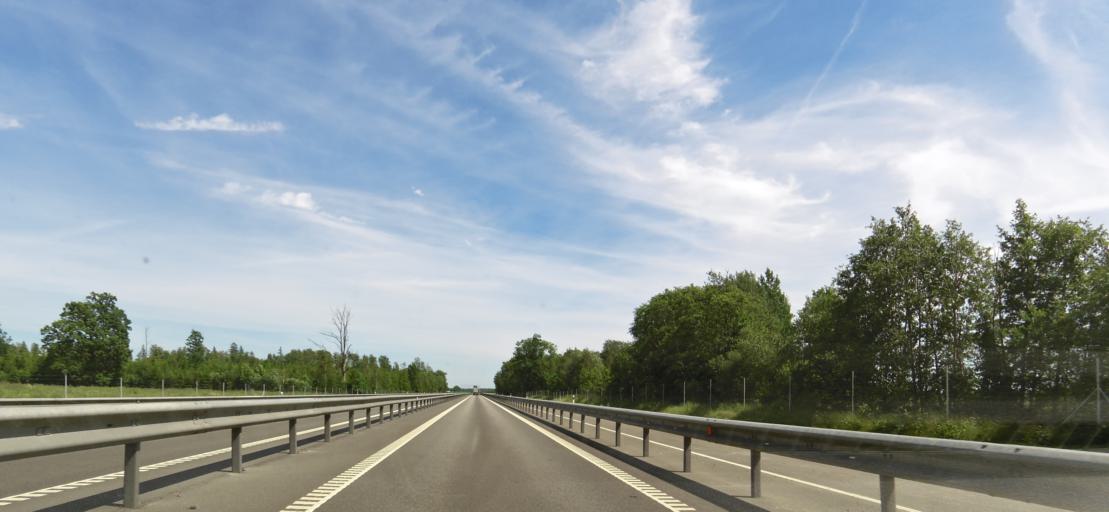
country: LT
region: Panevezys
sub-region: Panevezys City
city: Panevezys
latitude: 55.8027
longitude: 24.3543
